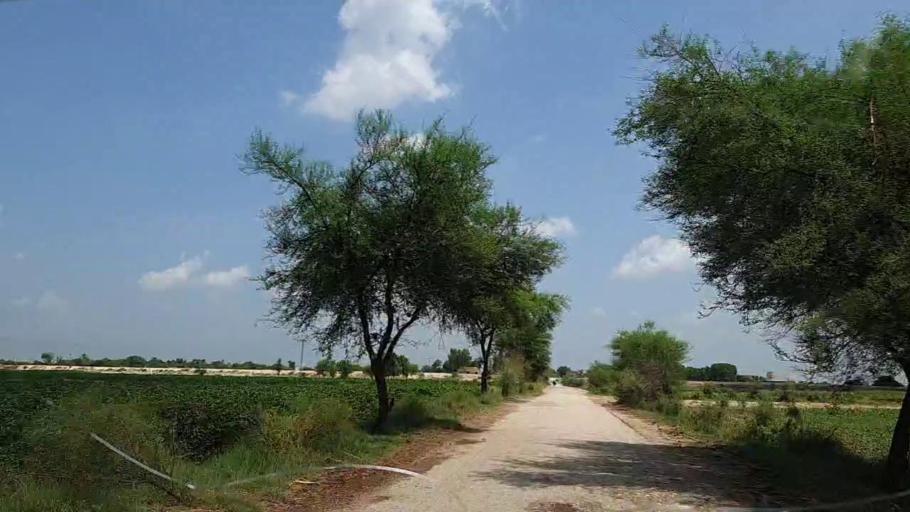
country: PK
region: Sindh
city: Tharu Shah
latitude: 26.9959
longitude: 68.0696
